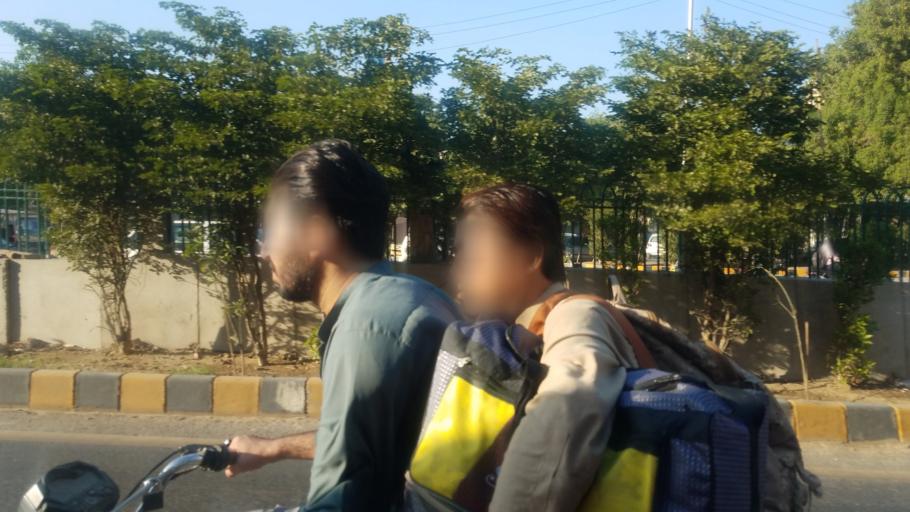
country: PK
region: Sindh
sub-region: Karachi District
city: Karachi
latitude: 24.8608
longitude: 67.0643
